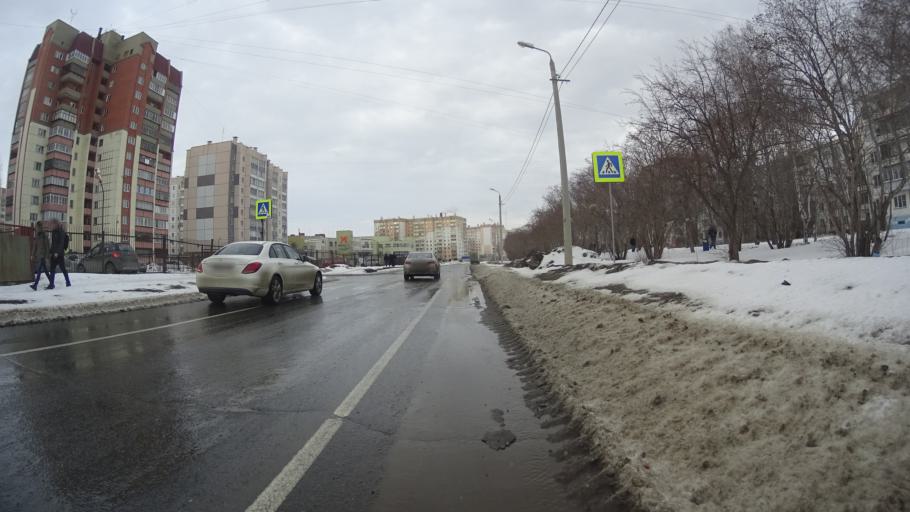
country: RU
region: Chelyabinsk
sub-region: Gorod Chelyabinsk
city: Chelyabinsk
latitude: 55.1965
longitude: 61.3214
